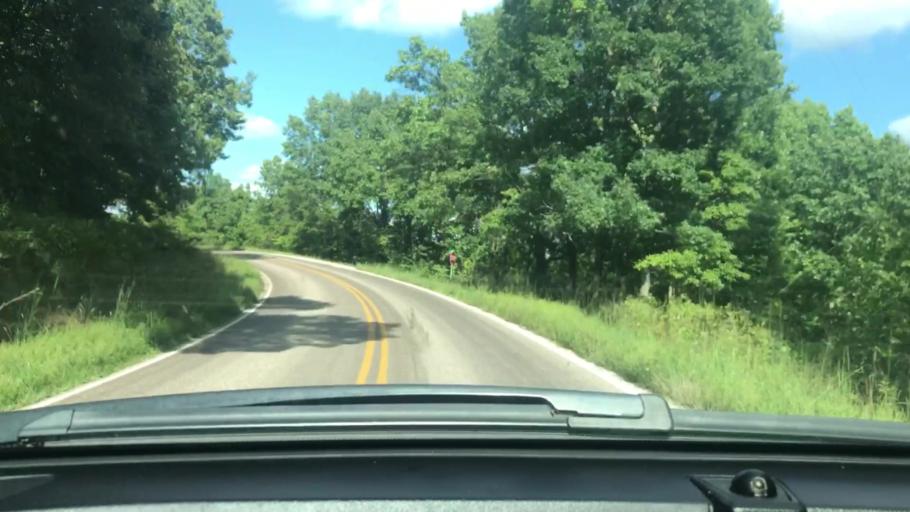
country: US
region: Missouri
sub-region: Wright County
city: Hartville
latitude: 37.3766
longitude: -92.3710
